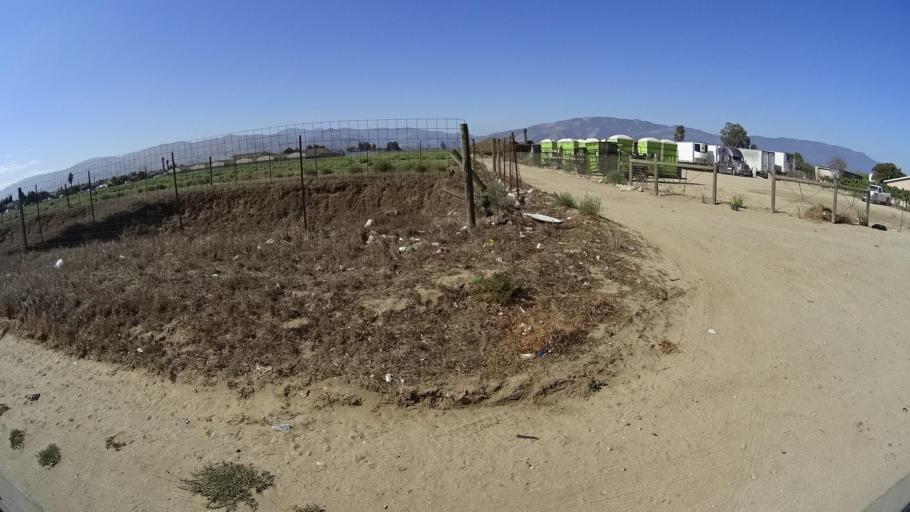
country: US
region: California
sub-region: Monterey County
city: Greenfield
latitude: 36.3212
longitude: -121.2546
